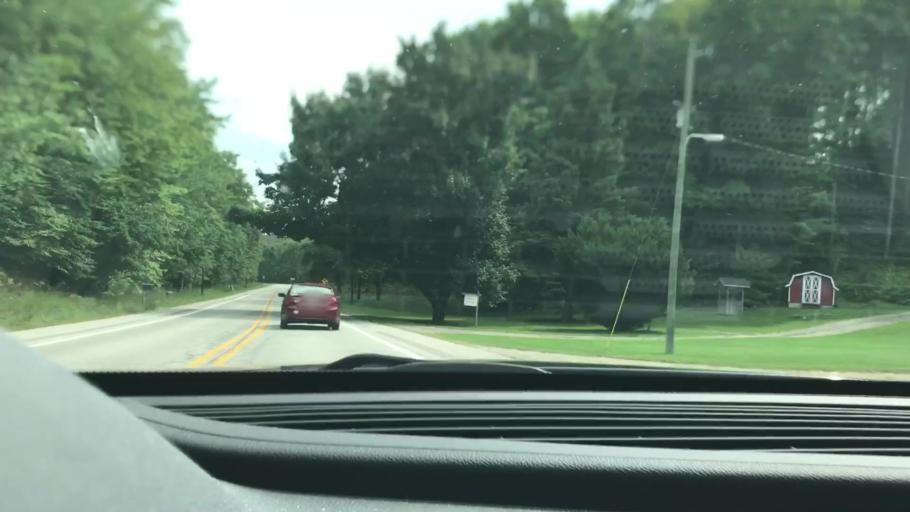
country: US
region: Michigan
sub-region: Antrim County
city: Bellaire
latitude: 45.0820
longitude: -85.2849
